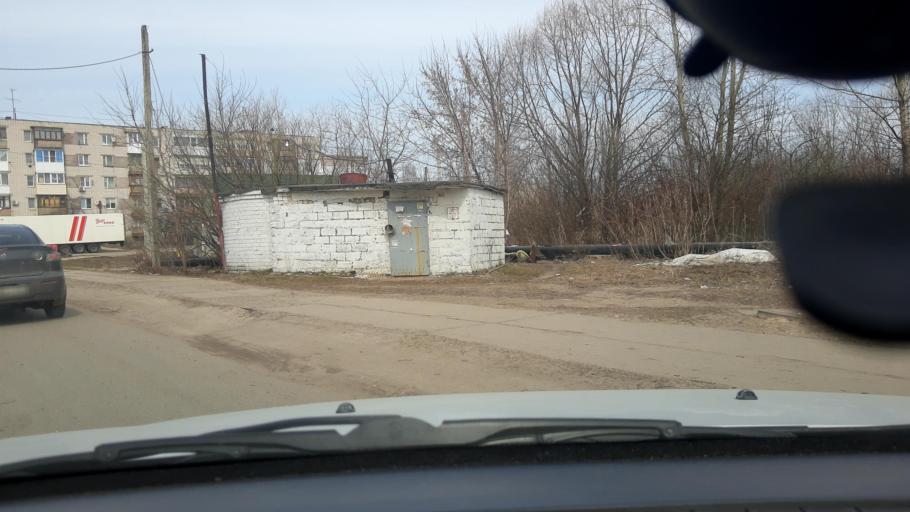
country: RU
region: Nizjnij Novgorod
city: Gidrotorf
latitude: 56.4635
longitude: 43.5382
